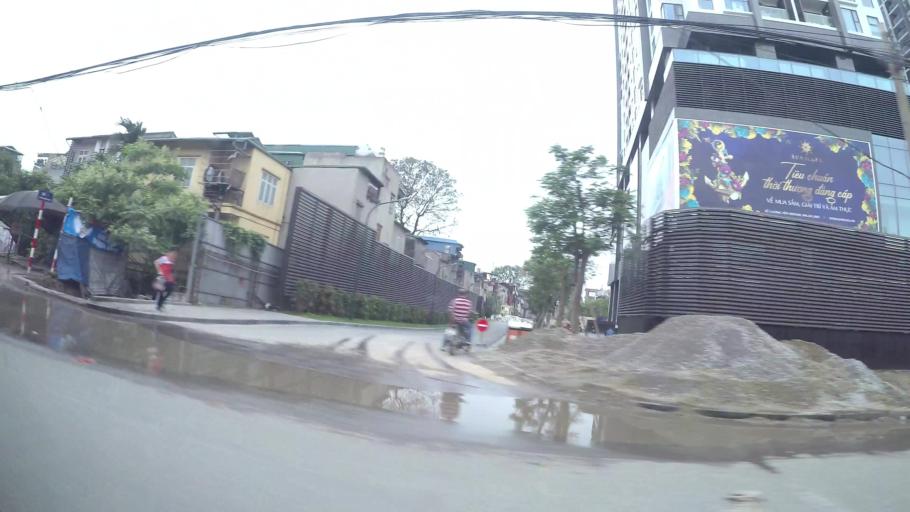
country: VN
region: Ha Noi
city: Hai BaTrung
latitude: 21.0104
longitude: 105.8645
